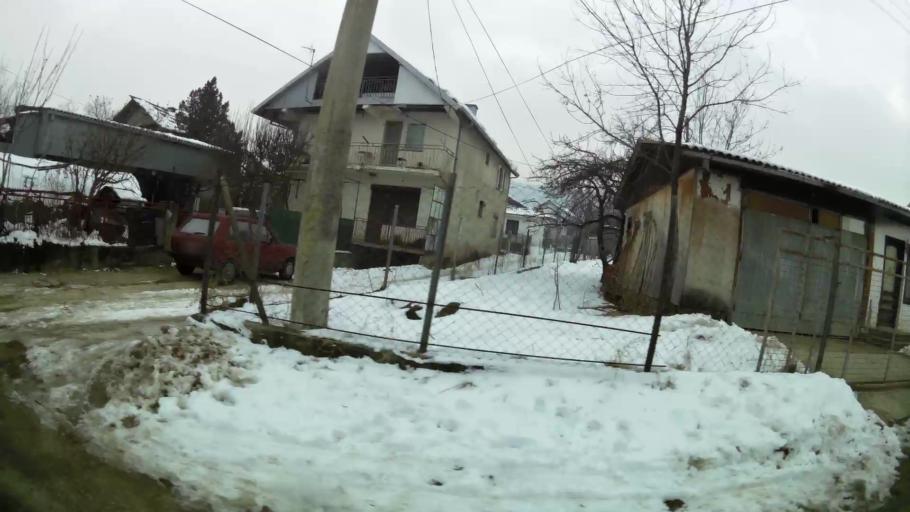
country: MK
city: Kondovo
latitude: 42.0493
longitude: 21.3435
